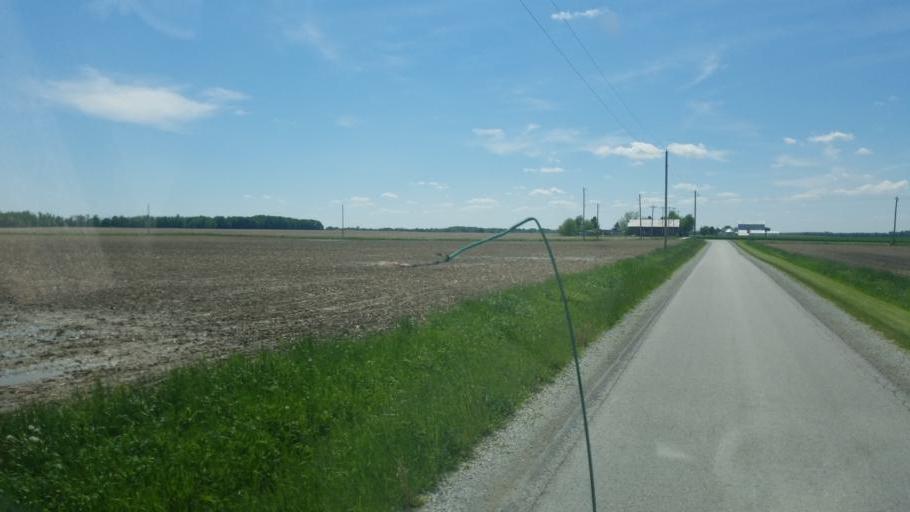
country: US
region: Ohio
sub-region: Crawford County
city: Bucyrus
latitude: 41.0083
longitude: -82.9564
